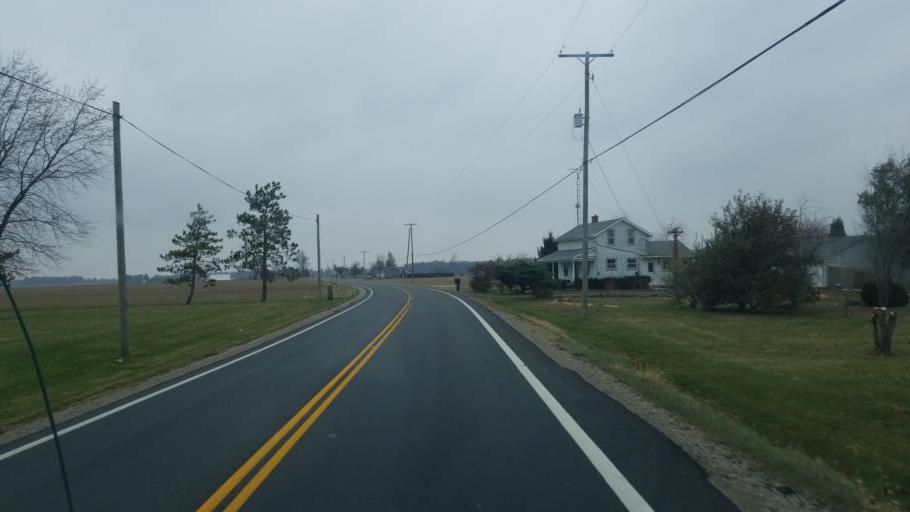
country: US
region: Ohio
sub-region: Crawford County
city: Crestline
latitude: 40.7990
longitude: -82.7883
